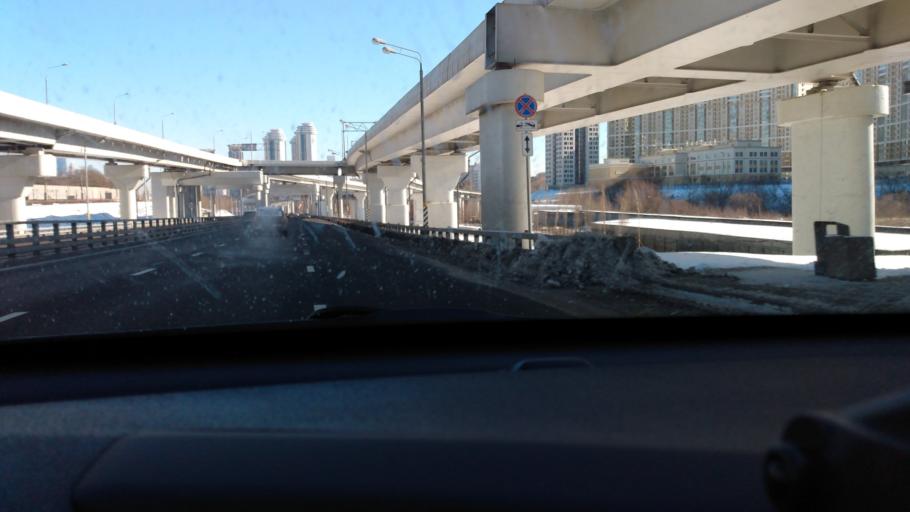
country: RU
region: Moscow
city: Matveyevskoye
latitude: 55.7038
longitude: 37.4836
